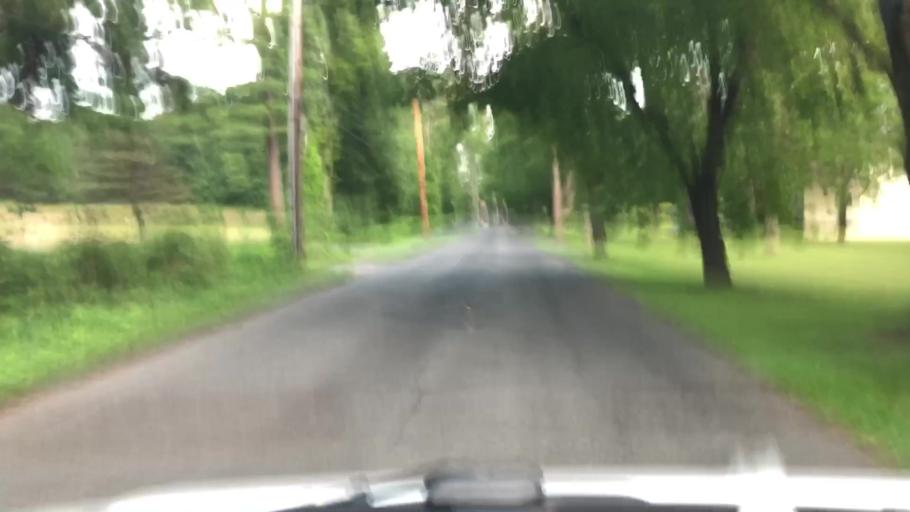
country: US
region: Massachusetts
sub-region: Berkshire County
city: Lee
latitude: 42.3027
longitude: -73.2655
